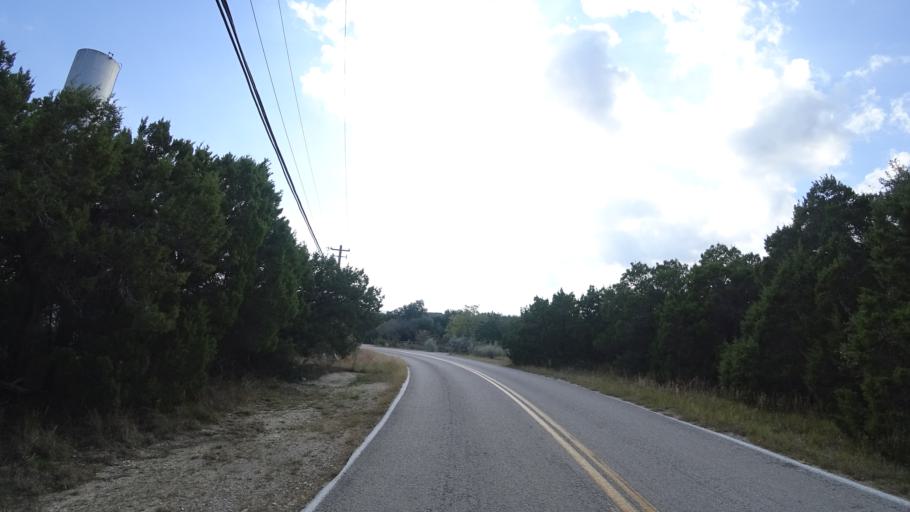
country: US
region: Texas
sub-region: Travis County
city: Barton Creek
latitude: 30.3090
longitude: -97.8661
